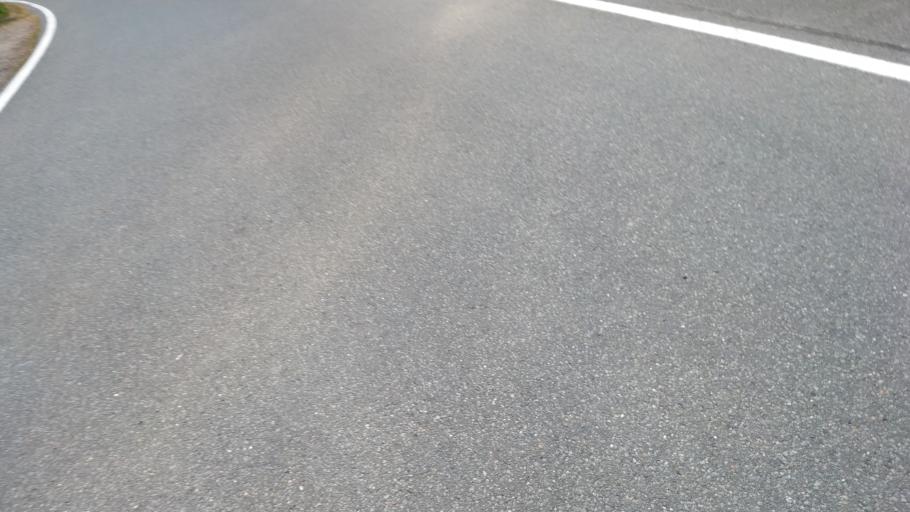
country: DE
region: Thuringia
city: Gopfersdorf
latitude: 50.9005
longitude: 12.6109
